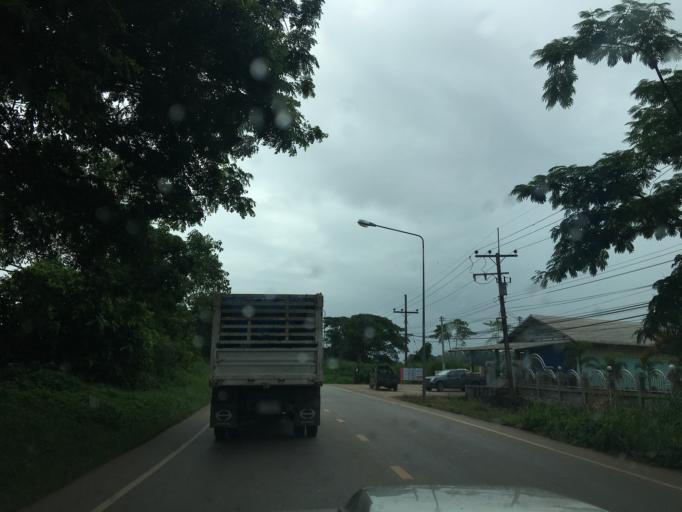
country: TH
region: Chiang Rai
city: Chiang Rai
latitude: 20.0054
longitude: 99.8882
